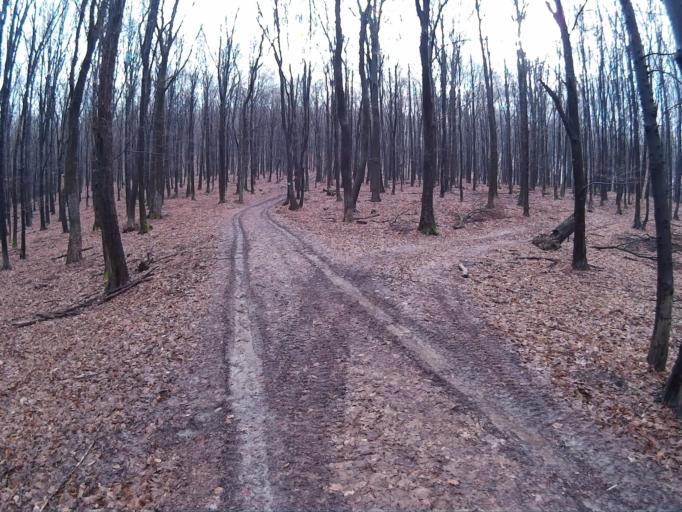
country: HU
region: Borsod-Abauj-Zemplen
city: Satoraljaujhely
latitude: 48.4174
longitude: 21.5824
